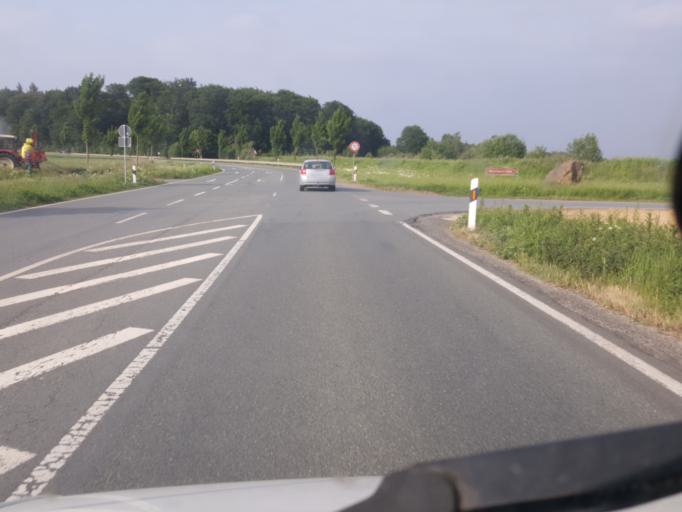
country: DE
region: Lower Saxony
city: Binnen
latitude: 52.6361
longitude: 9.1365
